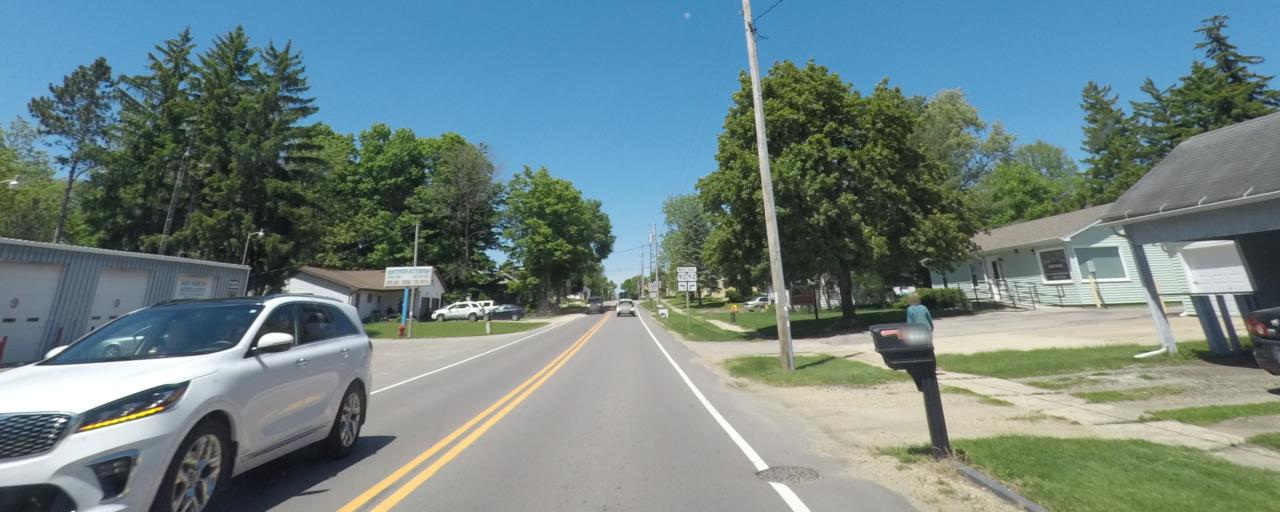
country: US
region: Wisconsin
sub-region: Green County
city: Brooklyn
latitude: 42.8511
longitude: -89.3691
